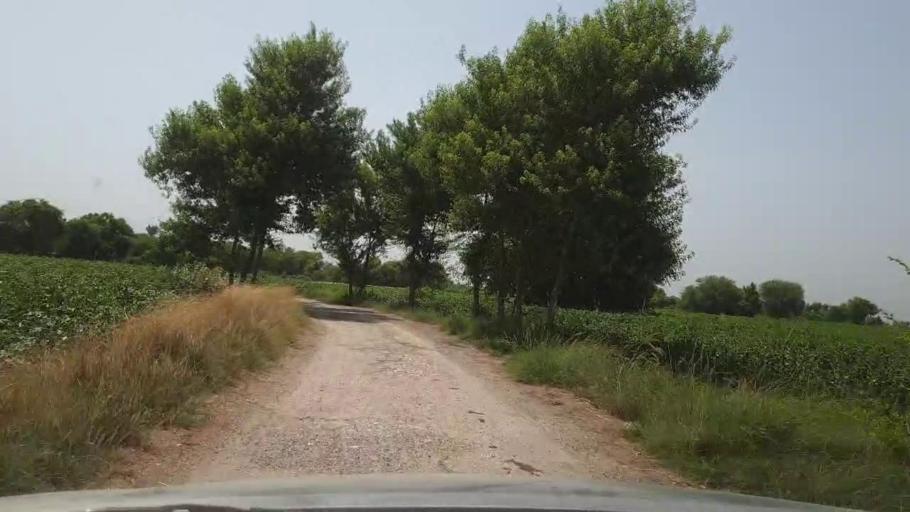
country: PK
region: Sindh
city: Pano Aqil
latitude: 27.7944
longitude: 69.2425
